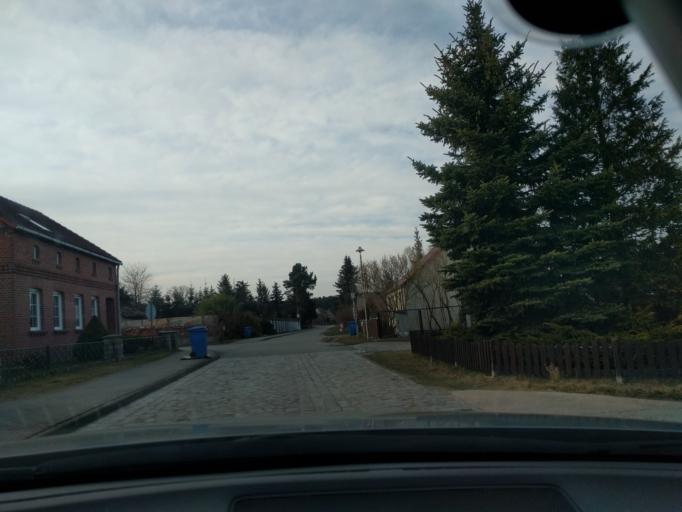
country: DE
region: Saxony-Anhalt
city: Sandau
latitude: 52.8197
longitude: 11.9977
